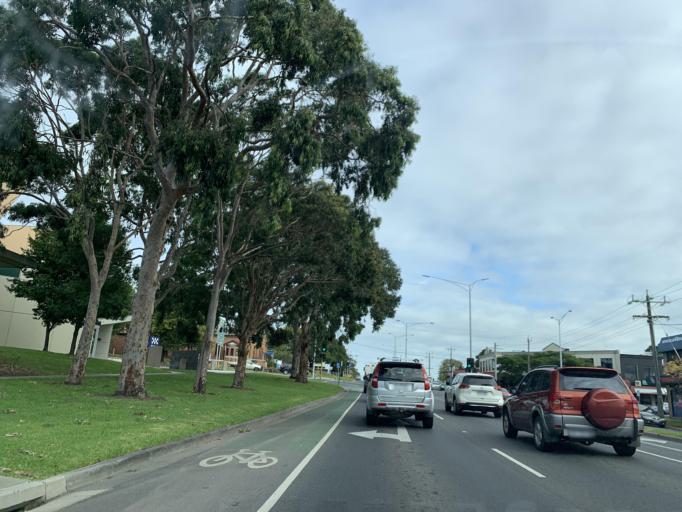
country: AU
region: Victoria
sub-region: Casey
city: Cranbourne
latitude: -38.1132
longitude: 145.2837
